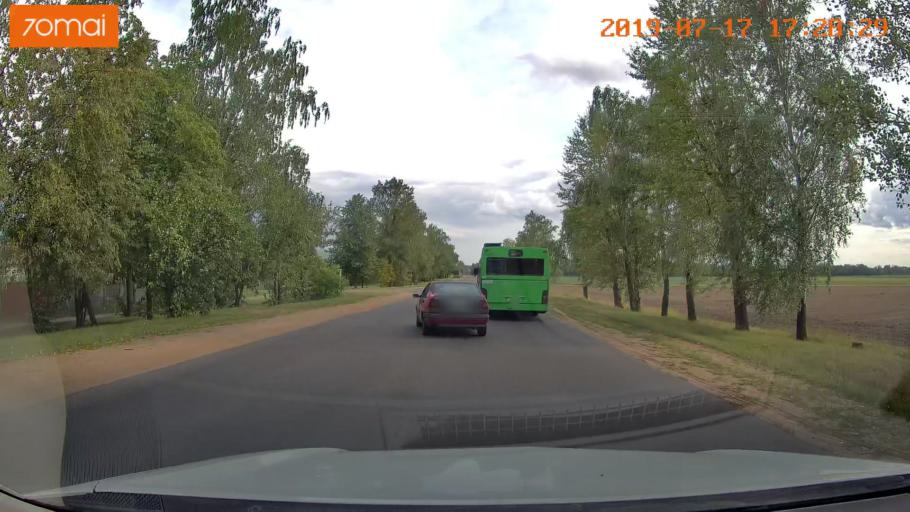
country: BY
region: Mogilev
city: Babruysk
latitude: 53.1294
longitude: 29.1667
